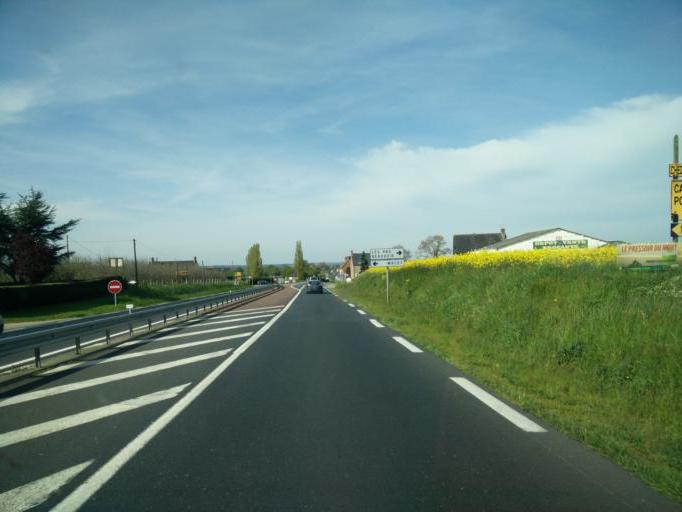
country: FR
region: Lower Normandy
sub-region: Departement de la Manche
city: Pontorson
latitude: 48.5785
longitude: -1.4463
